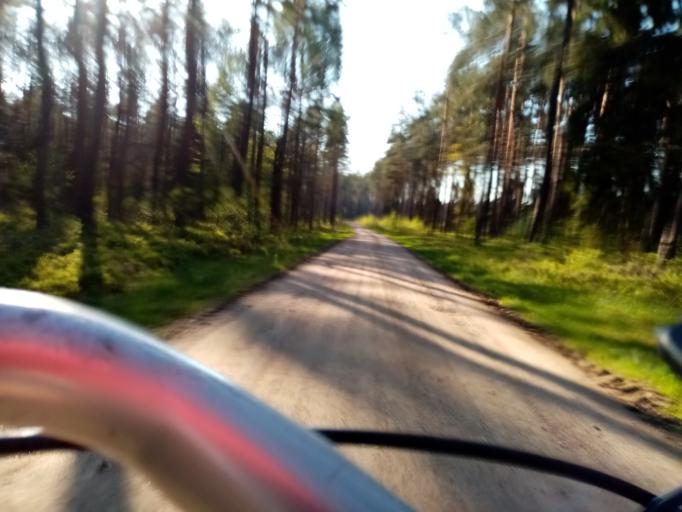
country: PL
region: Kujawsko-Pomorskie
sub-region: Powiat brodnicki
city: Gorzno
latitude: 53.1584
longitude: 19.6922
